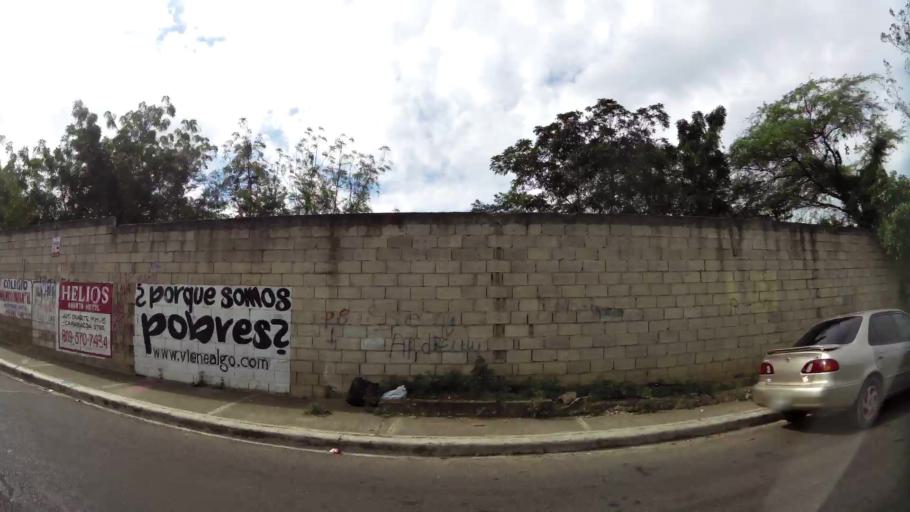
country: DO
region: Santiago
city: Santiago de los Caballeros
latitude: 19.4264
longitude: -70.6663
